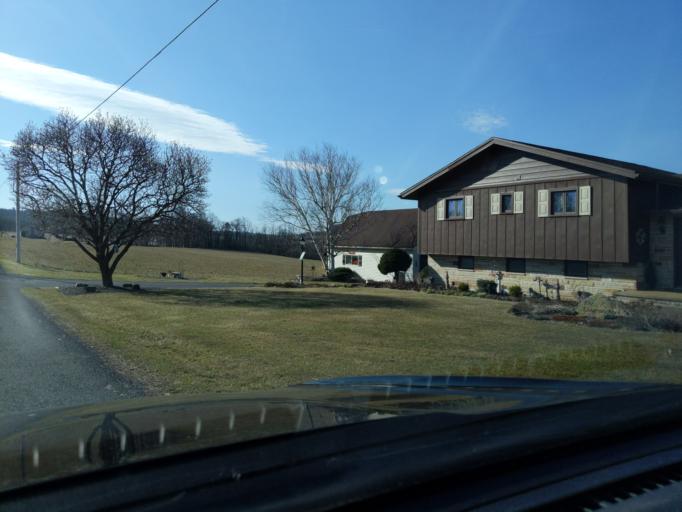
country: US
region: Pennsylvania
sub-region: Blair County
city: Martinsburg
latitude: 40.3961
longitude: -78.2758
